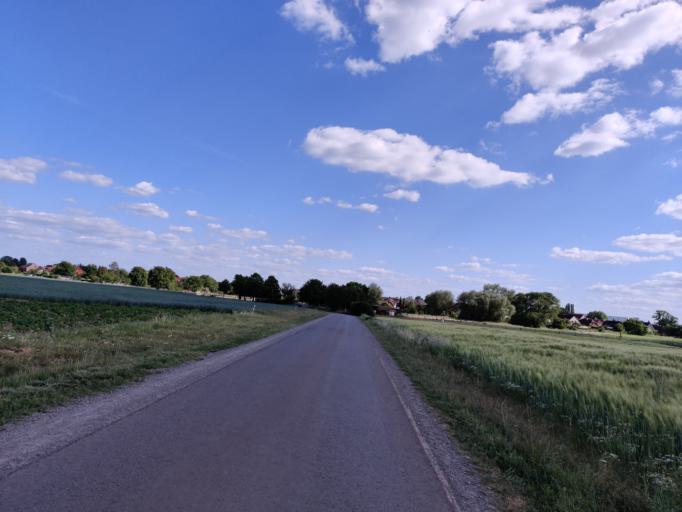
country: DE
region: Lower Saxony
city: Wunstorf
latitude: 52.4331
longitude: 9.4667
